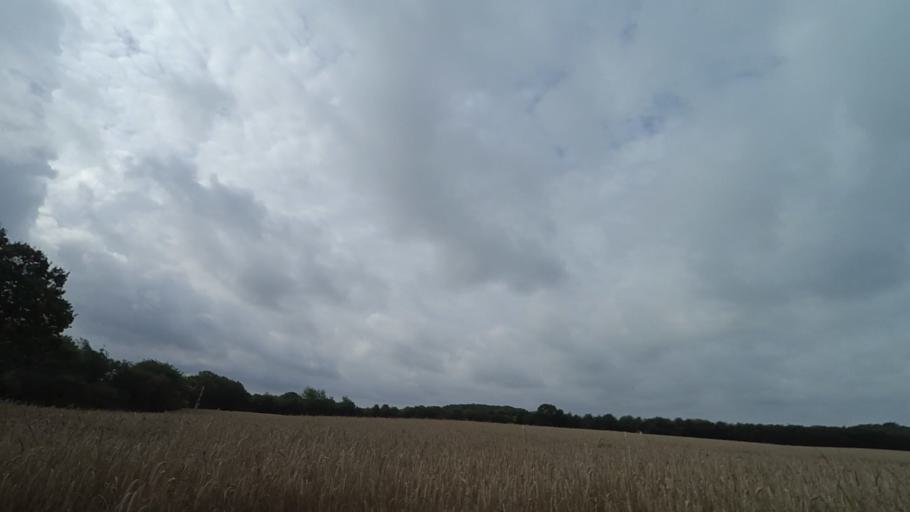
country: DK
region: Central Jutland
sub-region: Syddjurs Kommune
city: Ryomgard
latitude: 56.3987
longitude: 10.4961
